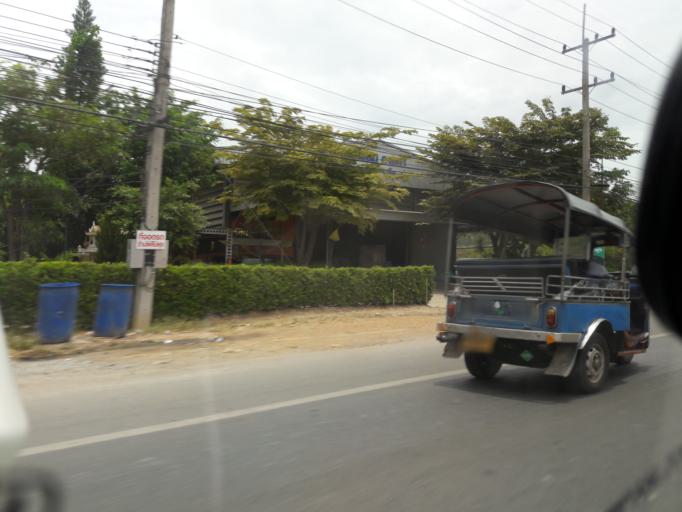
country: TH
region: Ratchaburi
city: Damnoen Saduak
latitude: 13.5622
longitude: 99.9692
